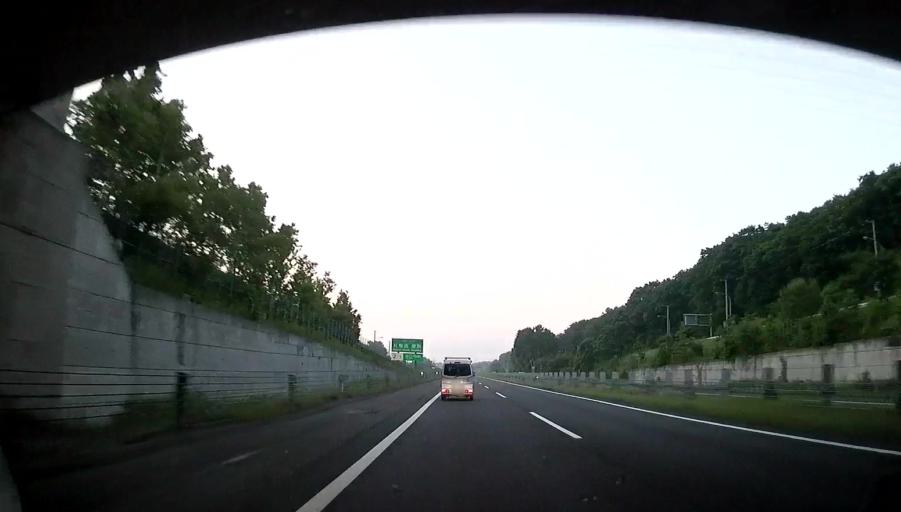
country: JP
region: Hokkaido
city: Kitahiroshima
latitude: 43.0018
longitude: 141.4676
